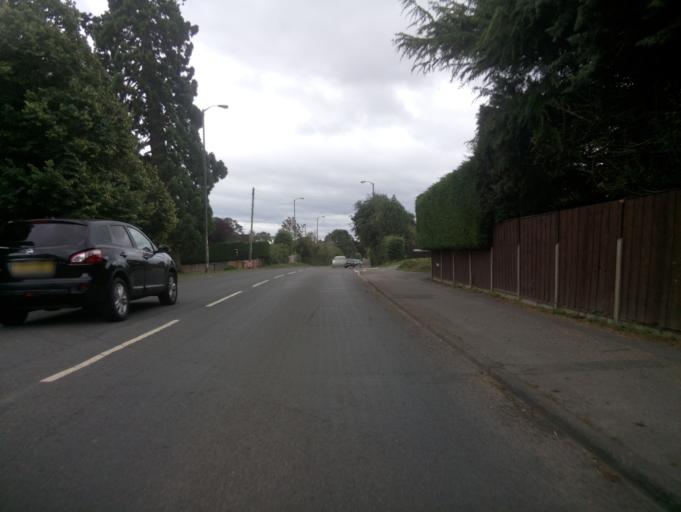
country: GB
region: England
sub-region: Worcestershire
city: Kempsey
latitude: 52.1454
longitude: -2.2156
